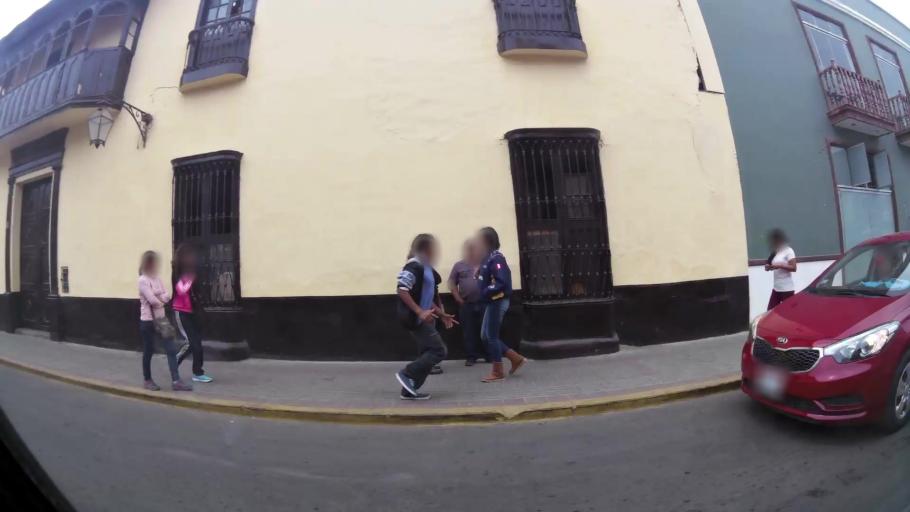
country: PE
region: La Libertad
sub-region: Provincia de Trujillo
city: Trujillo
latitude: -8.1098
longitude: -79.0298
